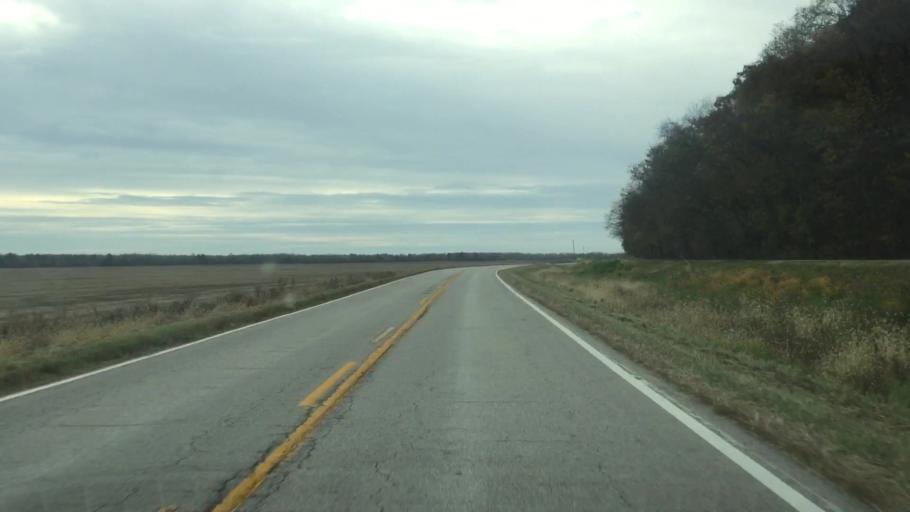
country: US
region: Missouri
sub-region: Gasconade County
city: Hermann
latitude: 38.7039
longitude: -91.5618
